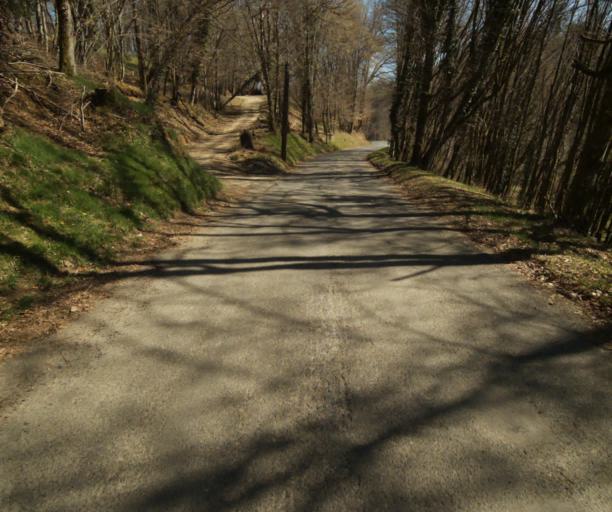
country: FR
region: Limousin
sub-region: Departement de la Correze
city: Naves
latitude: 45.3093
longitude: 1.7221
